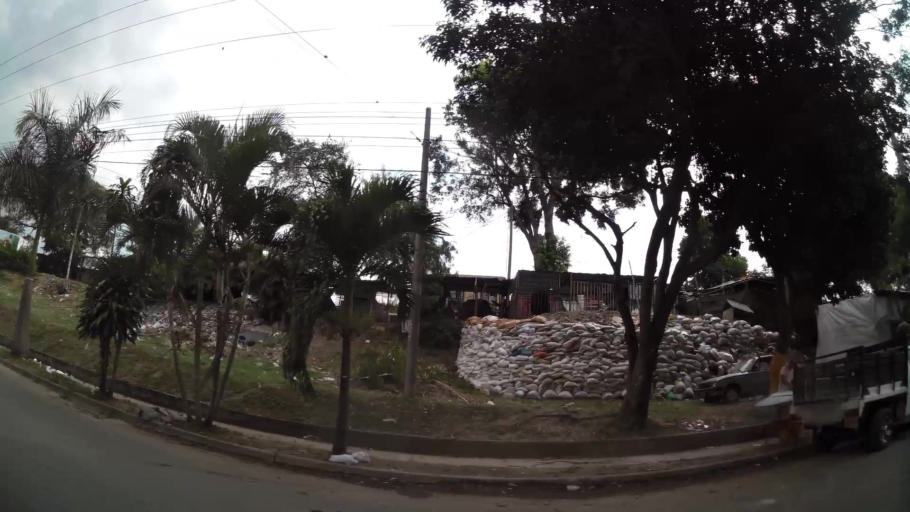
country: CO
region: Valle del Cauca
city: Cali
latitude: 3.4950
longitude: -76.4856
